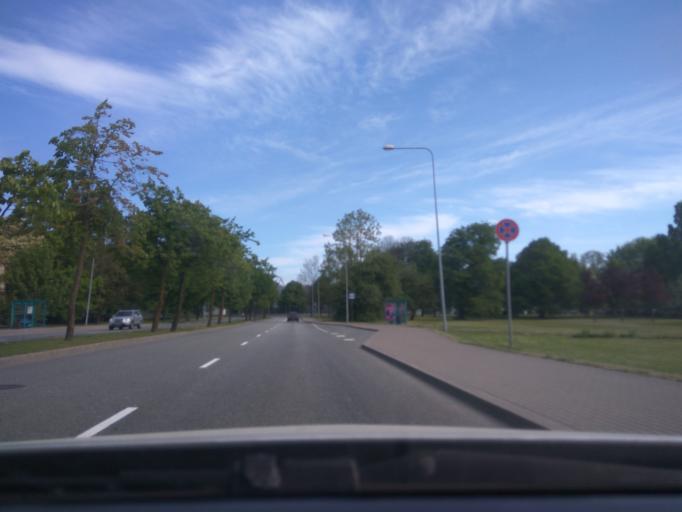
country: LV
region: Ventspils
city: Ventspils
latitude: 57.3882
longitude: 21.5829
